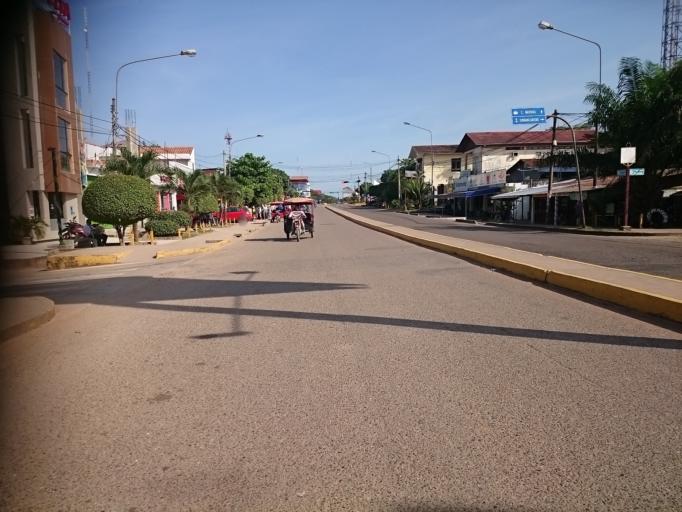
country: PE
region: Ucayali
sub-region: Provincia de Coronel Portillo
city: Puerto Callao
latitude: -8.3563
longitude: -74.5750
